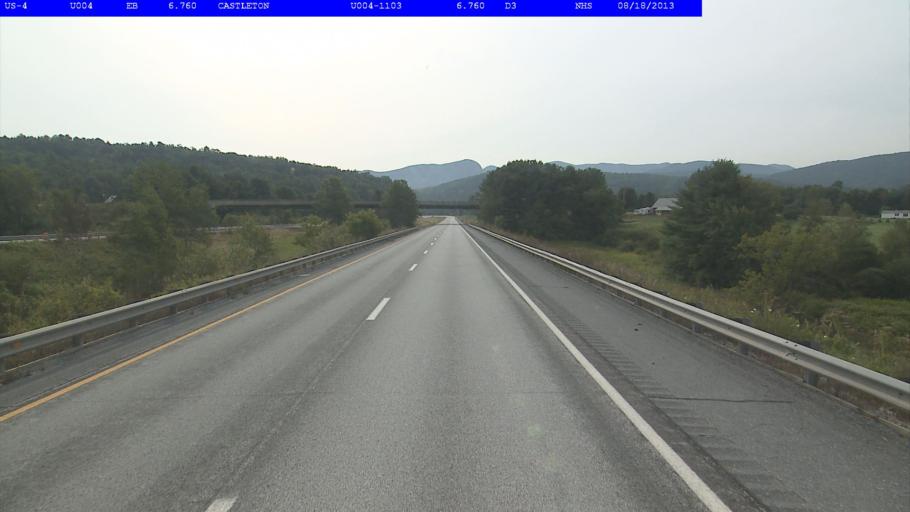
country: US
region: Vermont
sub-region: Rutland County
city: Castleton
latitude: 43.6203
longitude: -73.1841
